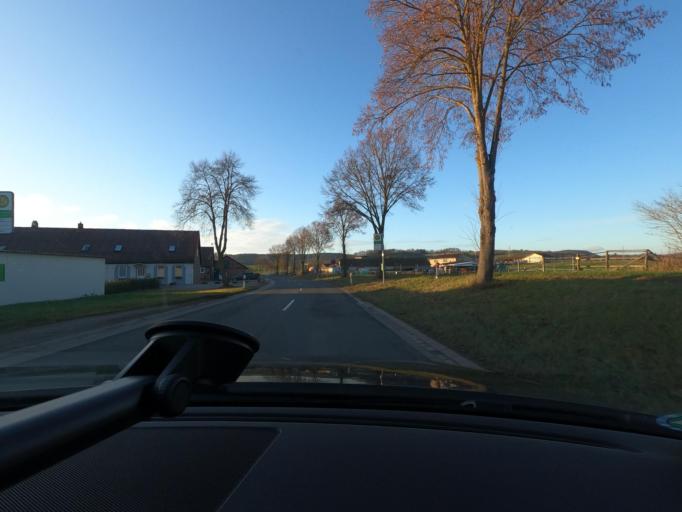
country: DE
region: Lower Saxony
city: Badenhausen
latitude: 51.7683
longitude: 10.1929
